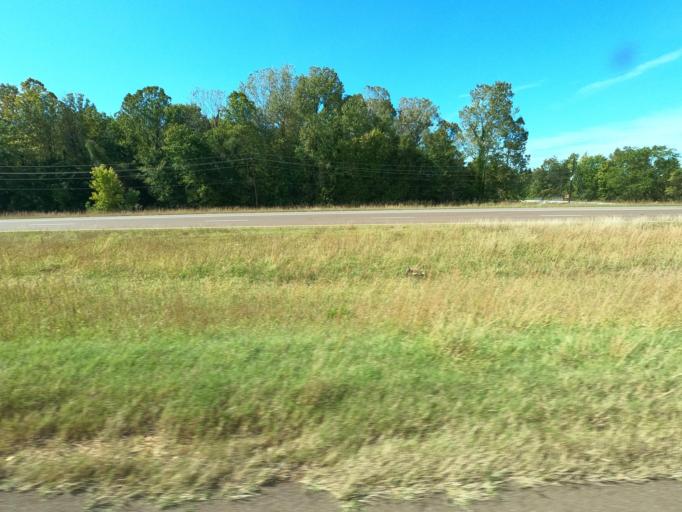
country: US
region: Tennessee
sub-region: Dyer County
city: Dyersburg
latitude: 36.0318
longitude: -89.3400
